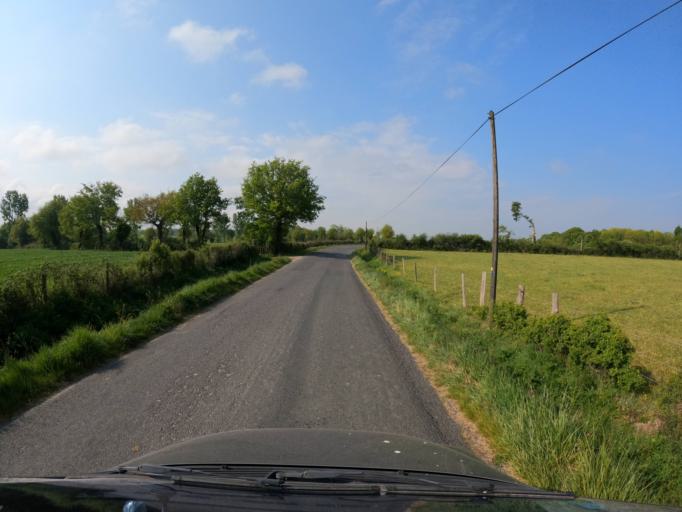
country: FR
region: Pays de la Loire
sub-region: Departement de Maine-et-Loire
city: Torfou
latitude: 47.0593
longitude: -1.0891
